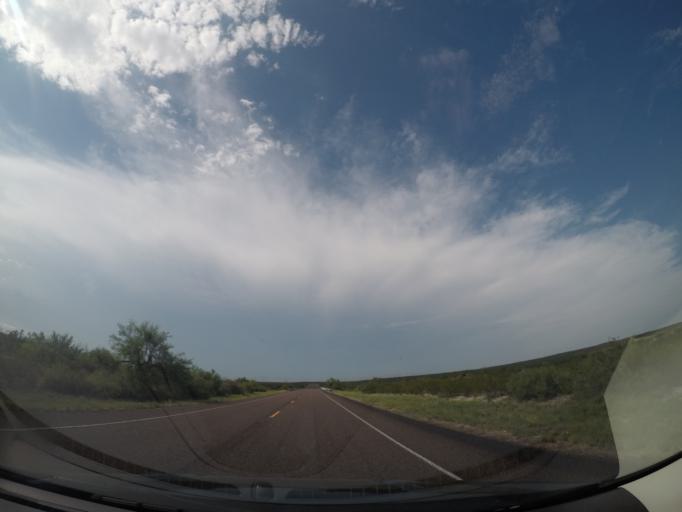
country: US
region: Texas
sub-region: Brewster County
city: Alpine
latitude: 29.7456
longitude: -103.1607
